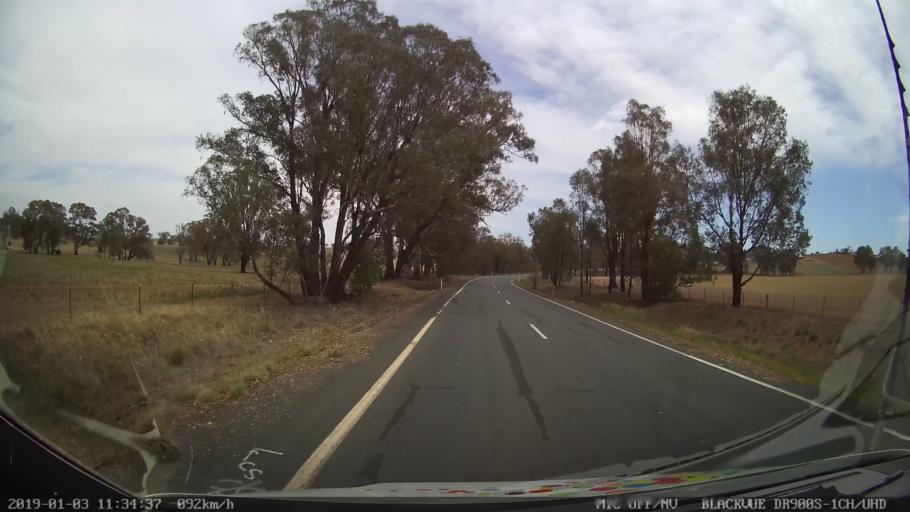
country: AU
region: New South Wales
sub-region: Weddin
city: Grenfell
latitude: -33.9328
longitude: 148.1619
